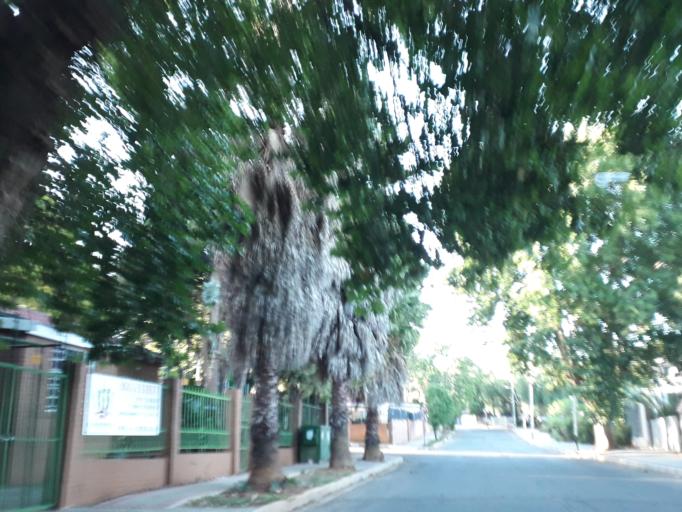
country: ZA
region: Gauteng
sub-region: City of Johannesburg Metropolitan Municipality
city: Johannesburg
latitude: -26.1740
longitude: 27.9933
